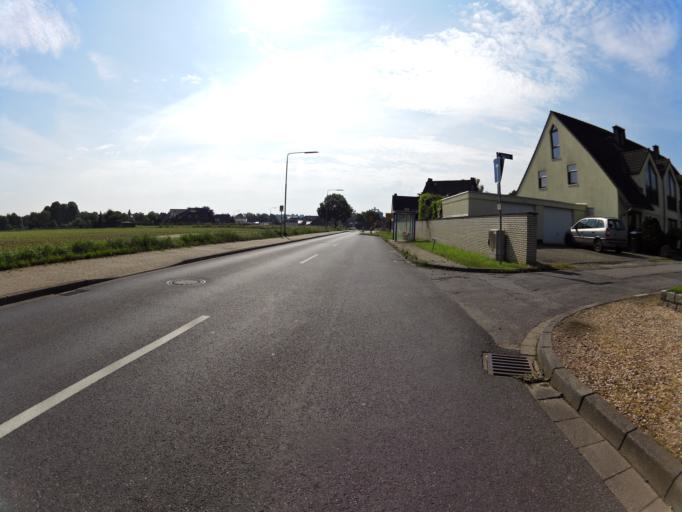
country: DE
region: North Rhine-Westphalia
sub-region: Regierungsbezirk Koln
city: Waldfeucht
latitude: 51.0520
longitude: 6.0309
